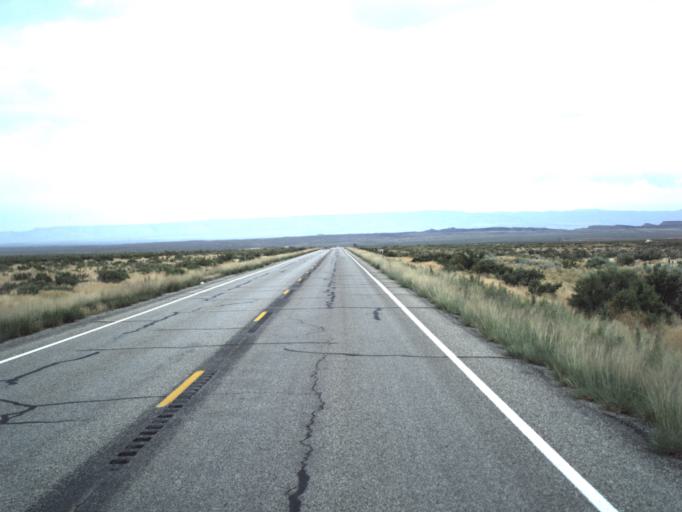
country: US
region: Utah
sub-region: Carbon County
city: East Carbon City
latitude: 39.5352
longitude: -110.5107
